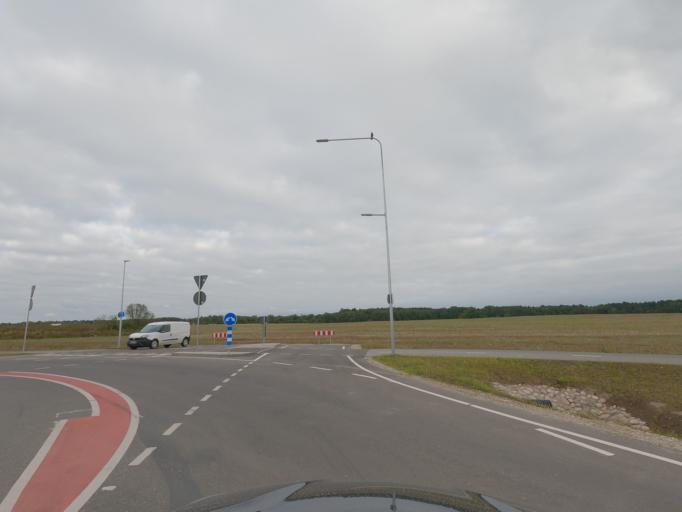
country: EE
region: Harju
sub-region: Kiili vald
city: Kiili
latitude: 59.3400
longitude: 24.8278
